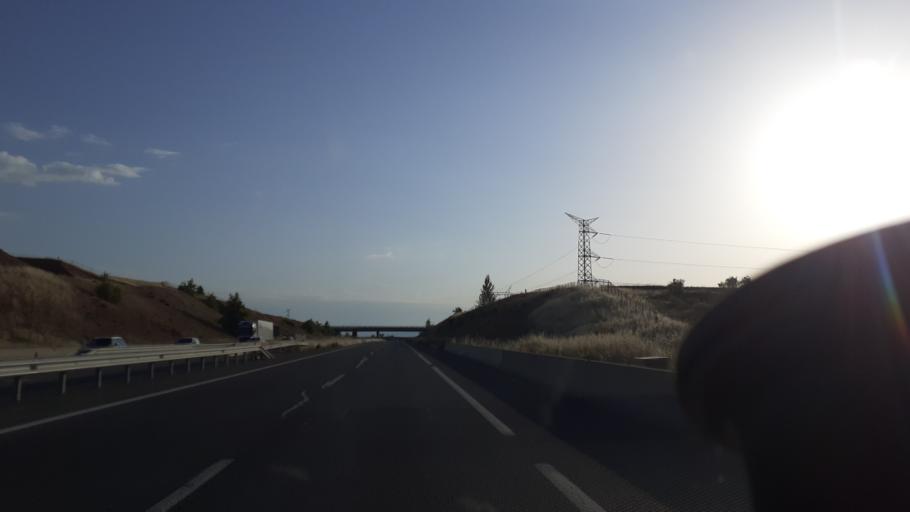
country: ES
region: Madrid
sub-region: Provincia de Madrid
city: El Molar
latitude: 40.7266
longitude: -3.5753
